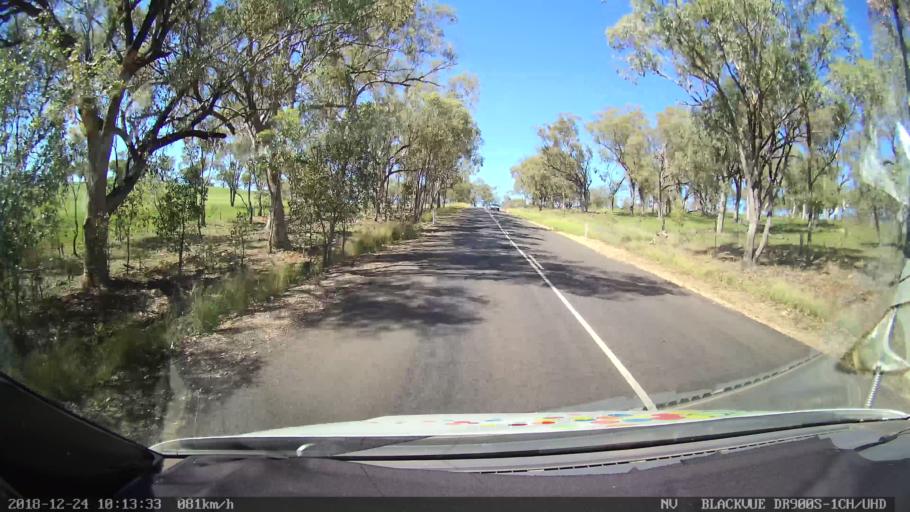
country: AU
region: New South Wales
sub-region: Liverpool Plains
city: Quirindi
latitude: -31.6911
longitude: 150.6389
